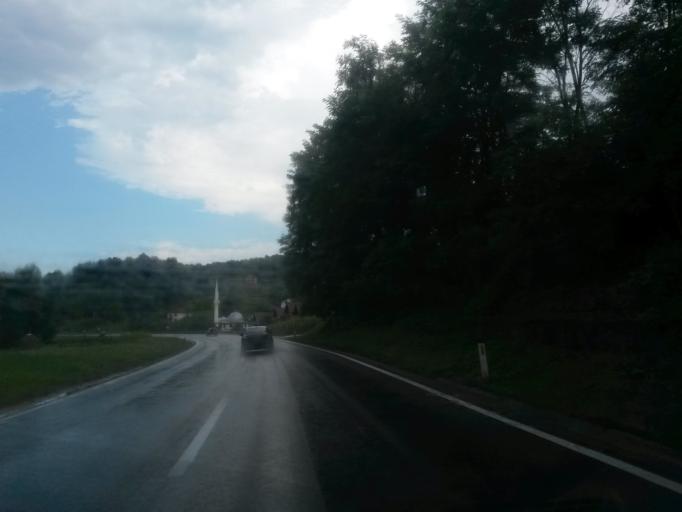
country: BA
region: Federation of Bosnia and Herzegovina
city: Lijesnica
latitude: 44.5066
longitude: 18.0815
